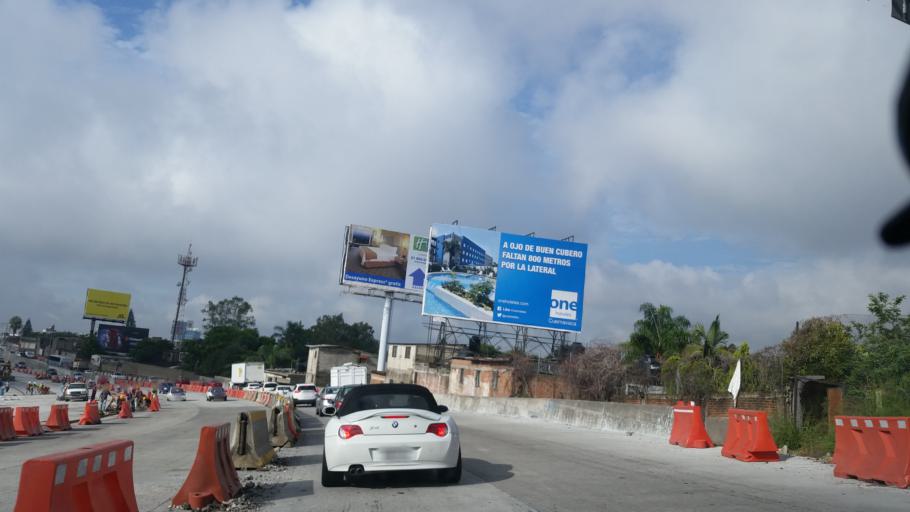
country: MX
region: Morelos
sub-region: Cuernavaca
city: Colonia los Cerritos
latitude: 18.9436
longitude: -99.1899
